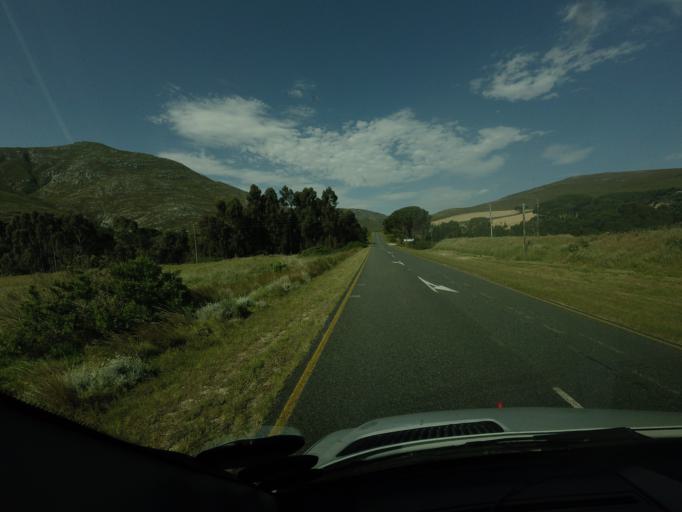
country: ZA
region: Western Cape
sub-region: Overberg District Municipality
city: Caledon
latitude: -34.4111
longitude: 19.5621
